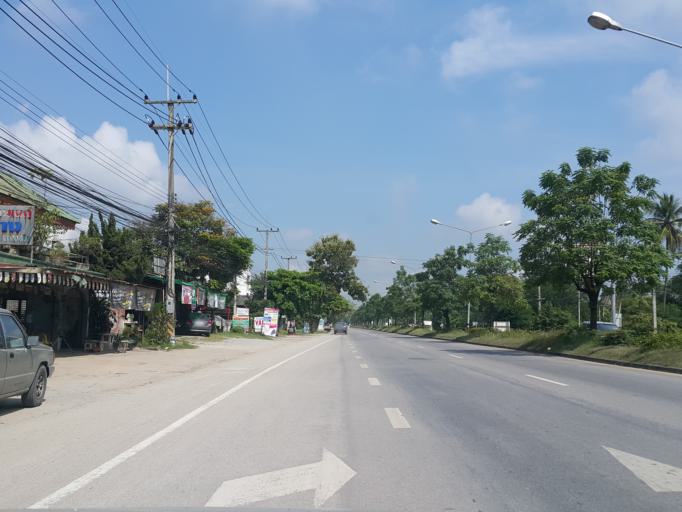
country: TH
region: Chiang Mai
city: San Sai
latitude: 18.9224
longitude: 98.9940
